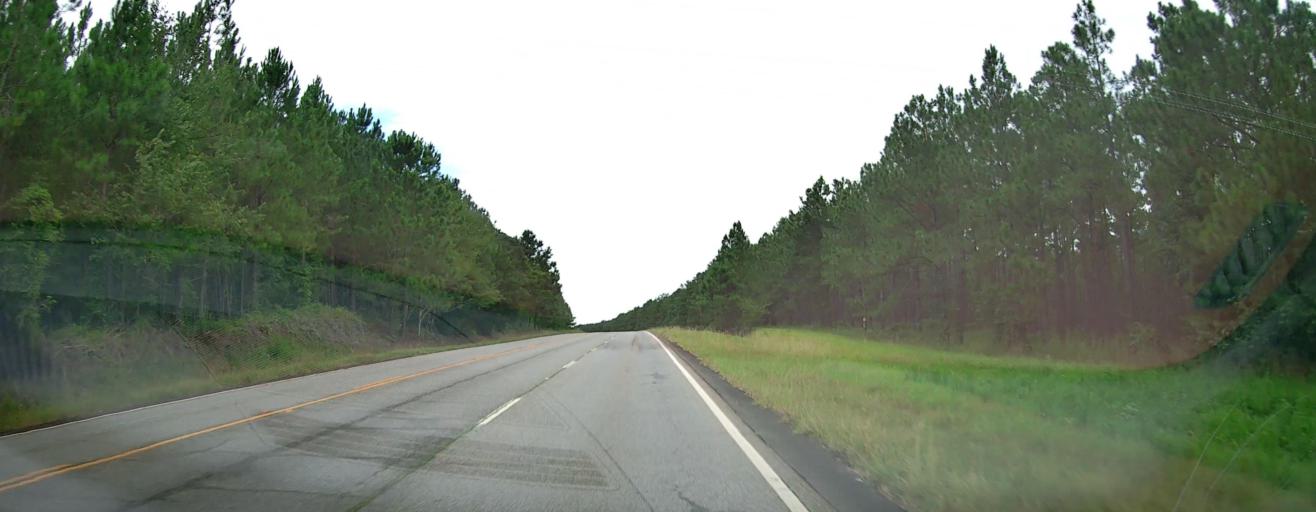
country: US
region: Georgia
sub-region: Marion County
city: Buena Vista
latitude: 32.2875
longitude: -84.4481
